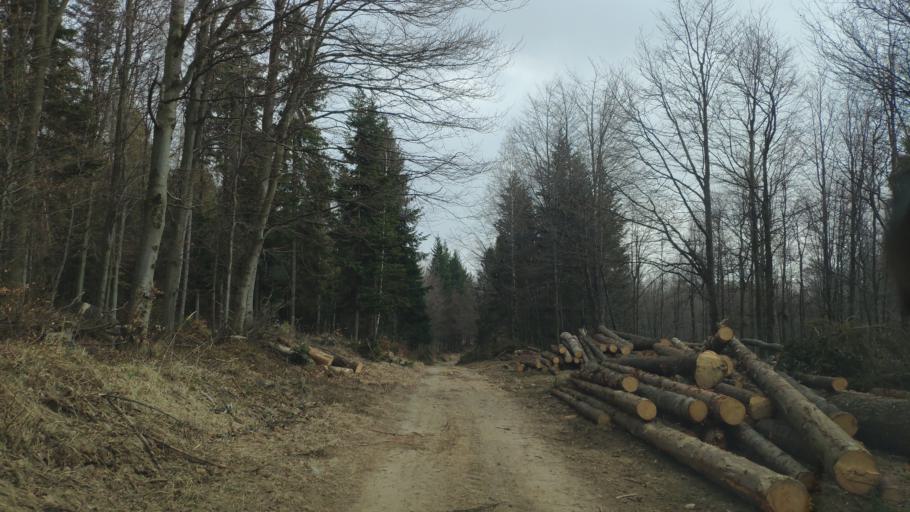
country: SK
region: Kosicky
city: Moldava nad Bodvou
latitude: 48.7451
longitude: 21.0417
